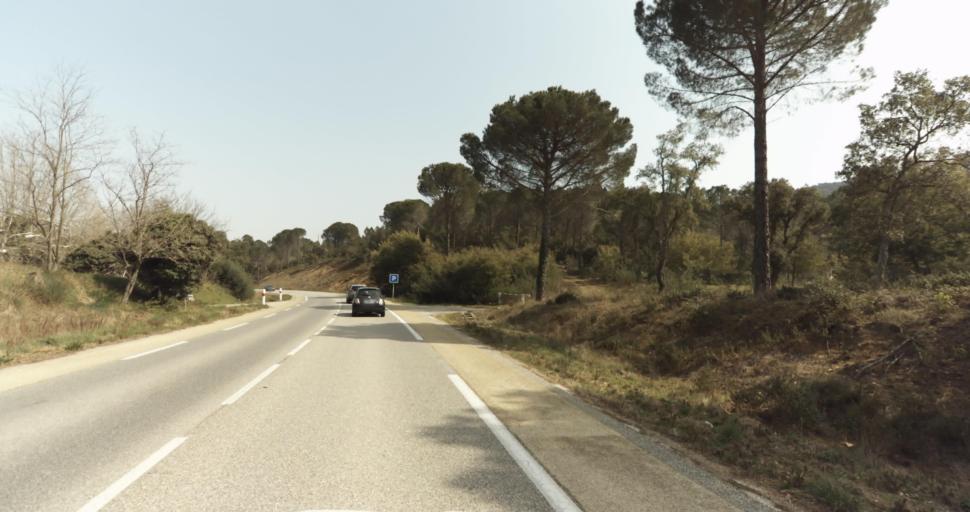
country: FR
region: Provence-Alpes-Cote d'Azur
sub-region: Departement du Var
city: Le Lavandou
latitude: 43.1906
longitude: 6.3728
